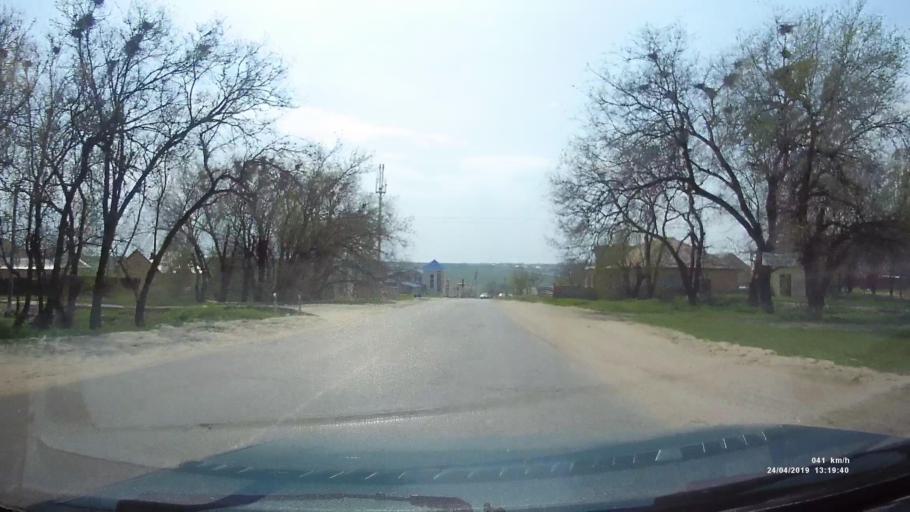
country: RU
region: Kalmykiya
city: Elista
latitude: 46.2989
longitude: 44.2893
